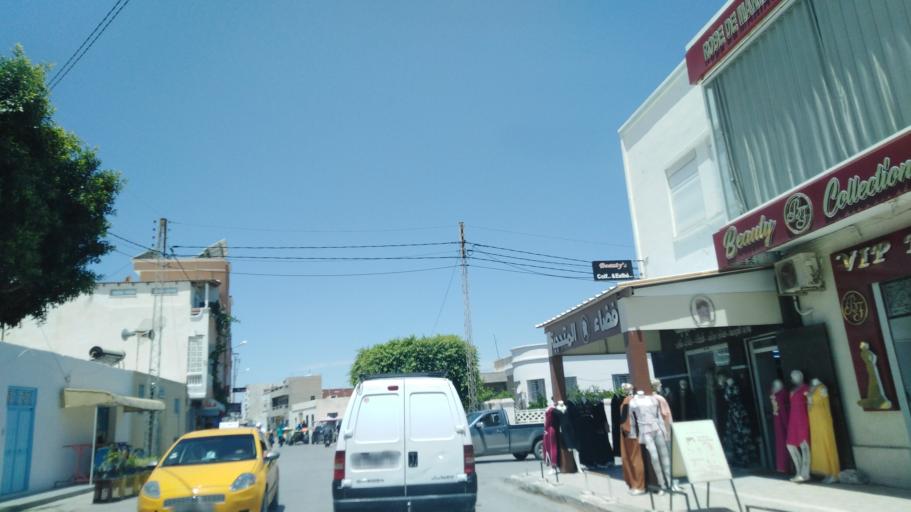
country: TN
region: Al Mahdiyah
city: Ksour Essaf
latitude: 35.4167
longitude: 10.9964
